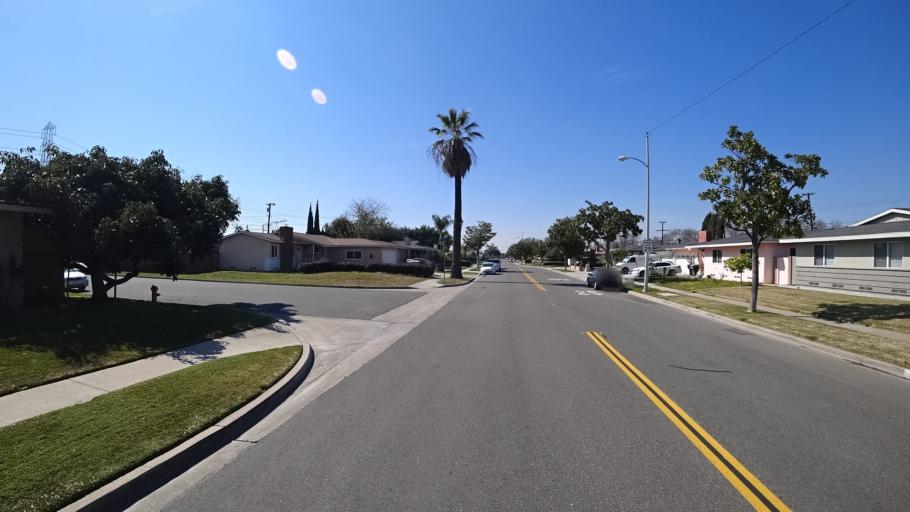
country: US
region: California
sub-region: Orange County
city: Garden Grove
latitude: 33.8084
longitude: -117.9450
